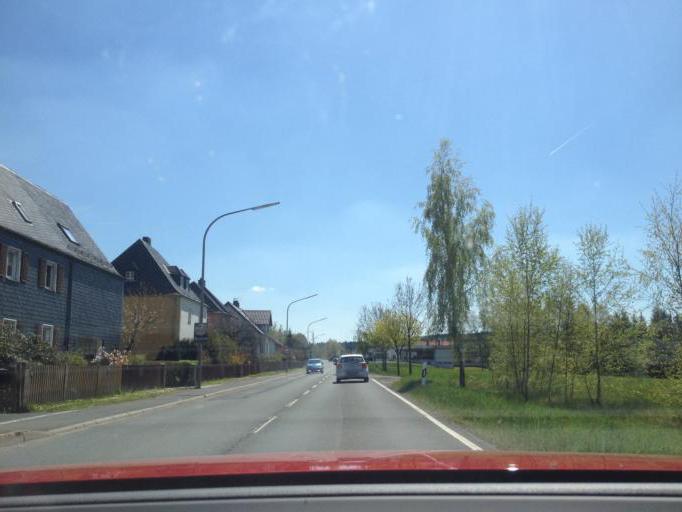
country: DE
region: Bavaria
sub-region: Upper Franconia
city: Schwarzenbach an der Saale
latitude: 50.2138
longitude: 11.9385
